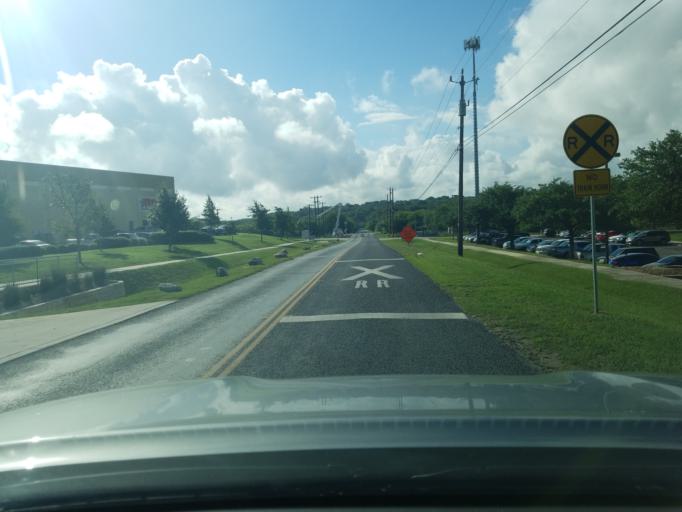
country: US
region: Texas
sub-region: Bexar County
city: Live Oak
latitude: 29.5988
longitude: -98.3634
